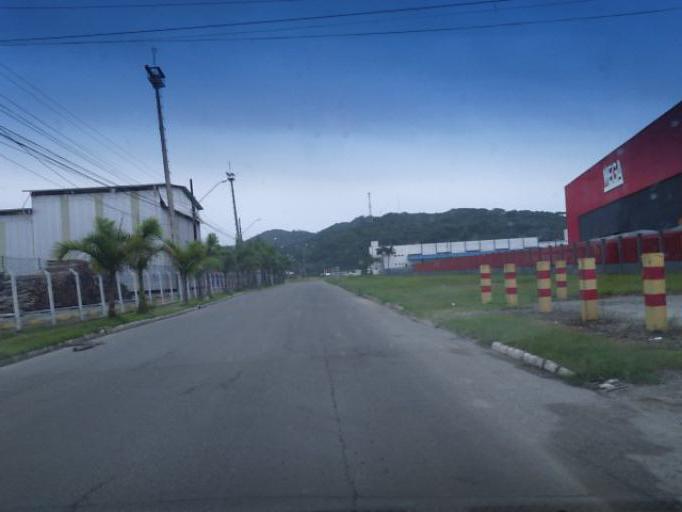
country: BR
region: Santa Catarina
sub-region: Itajai
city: Itajai
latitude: -26.9003
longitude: -48.7097
